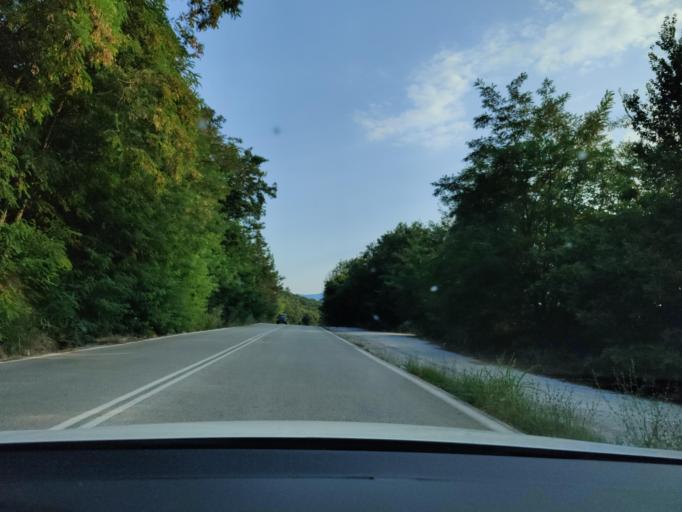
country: GR
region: East Macedonia and Thrace
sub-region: Nomos Kavalas
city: Zygos
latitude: 41.0062
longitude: 24.3822
